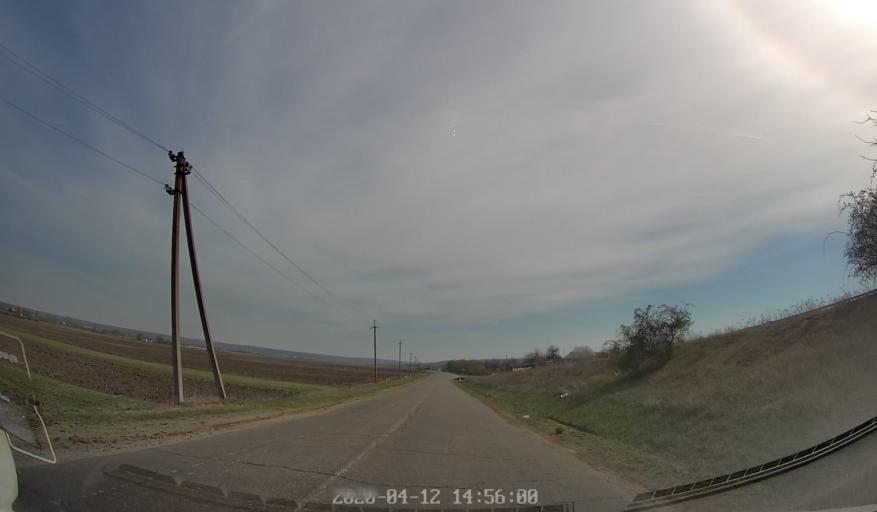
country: MD
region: Telenesti
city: Dubasari
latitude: 47.2658
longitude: 29.1263
